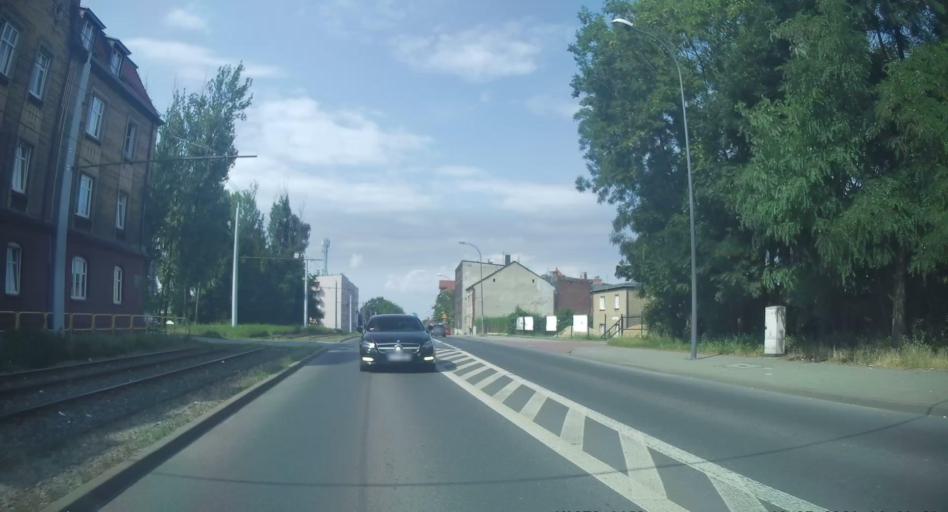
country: PL
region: Silesian Voivodeship
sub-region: Bytom
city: Bytom
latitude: 50.3219
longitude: 18.9268
